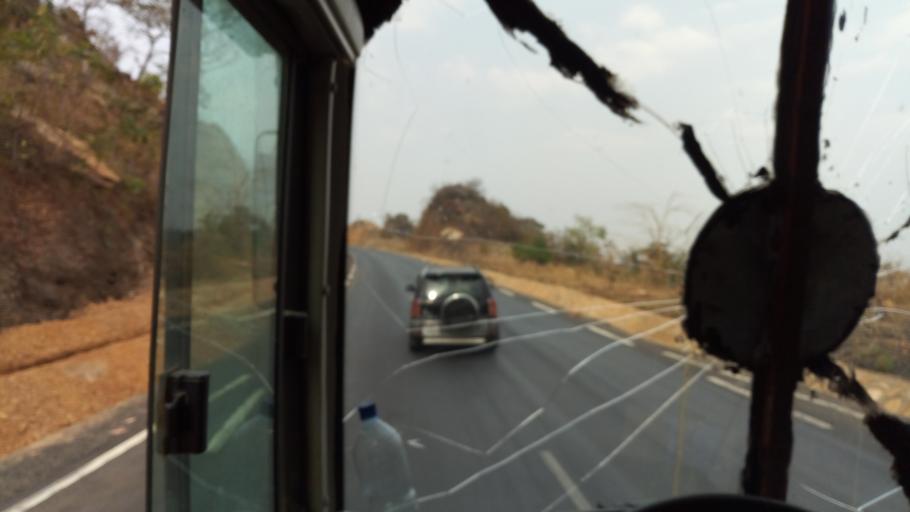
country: TG
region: Kara
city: Bafilo
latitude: 9.2703
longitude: 1.2356
